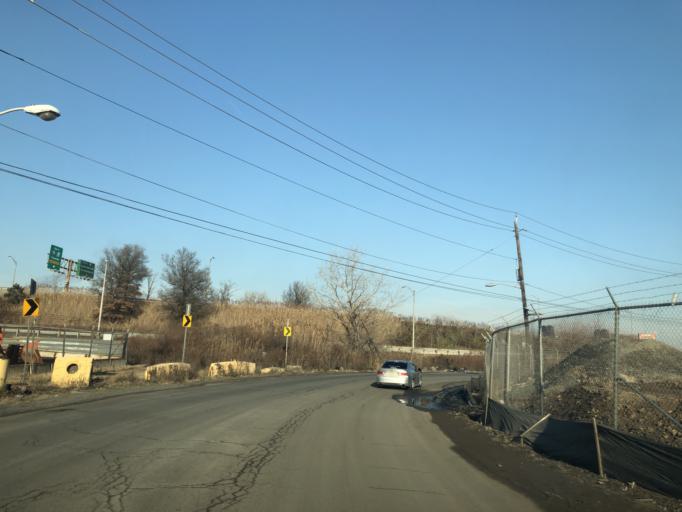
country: US
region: New Jersey
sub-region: Hudson County
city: Harrison
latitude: 40.7274
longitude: -74.1282
